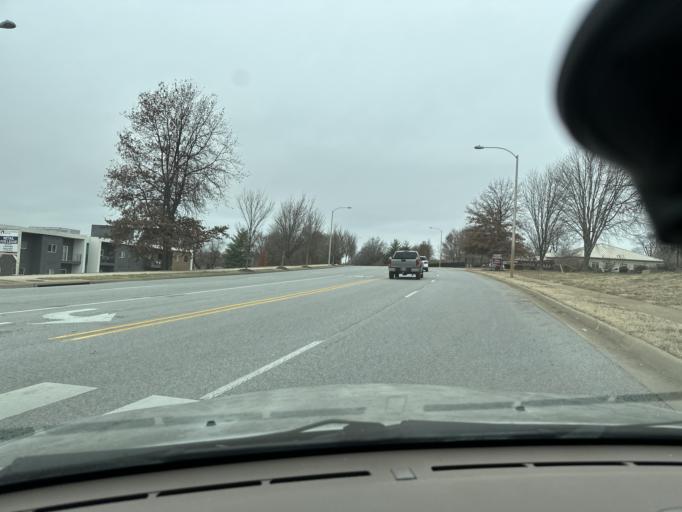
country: US
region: Arkansas
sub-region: Washington County
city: Johnson
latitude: 36.1250
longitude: -94.1564
